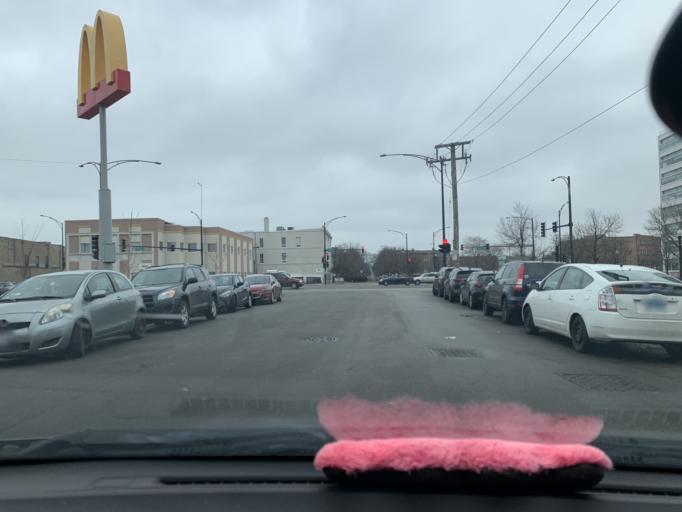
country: US
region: Illinois
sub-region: Cook County
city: Chicago
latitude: 41.8661
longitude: -87.6835
